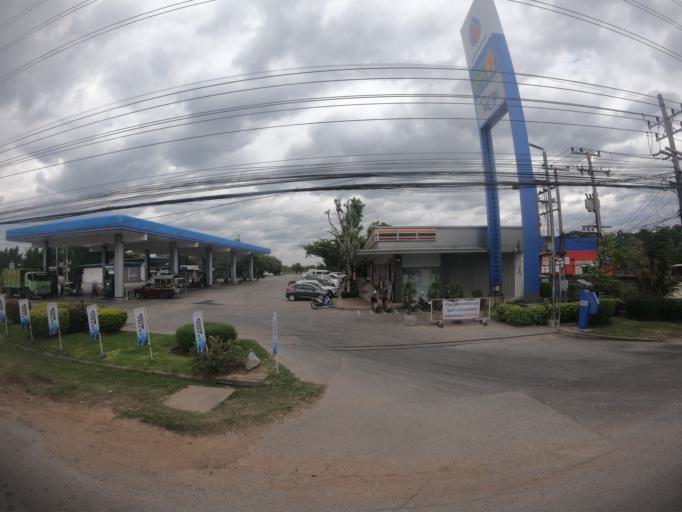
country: TH
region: Nakhon Ratchasima
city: Nakhon Ratchasima
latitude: 14.9385
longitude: 102.1329
